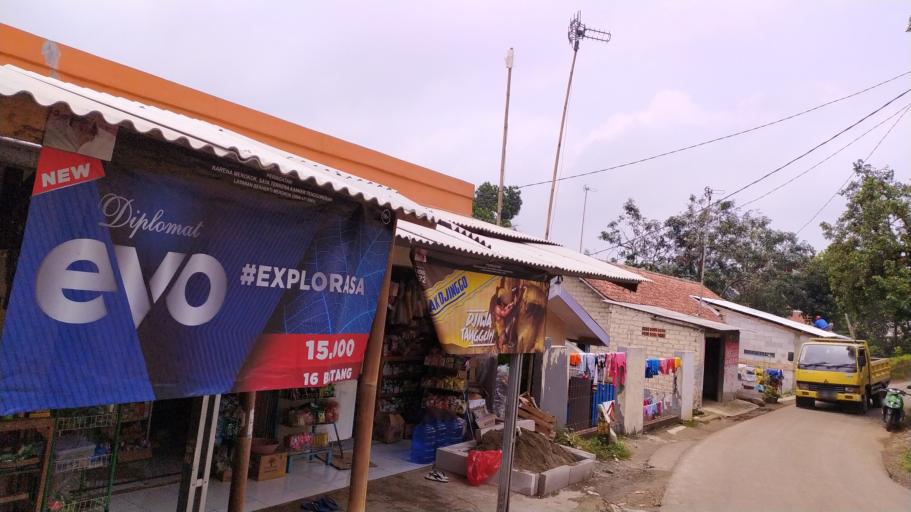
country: ID
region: West Java
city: Ciampea
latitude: -6.6292
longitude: 106.7112
